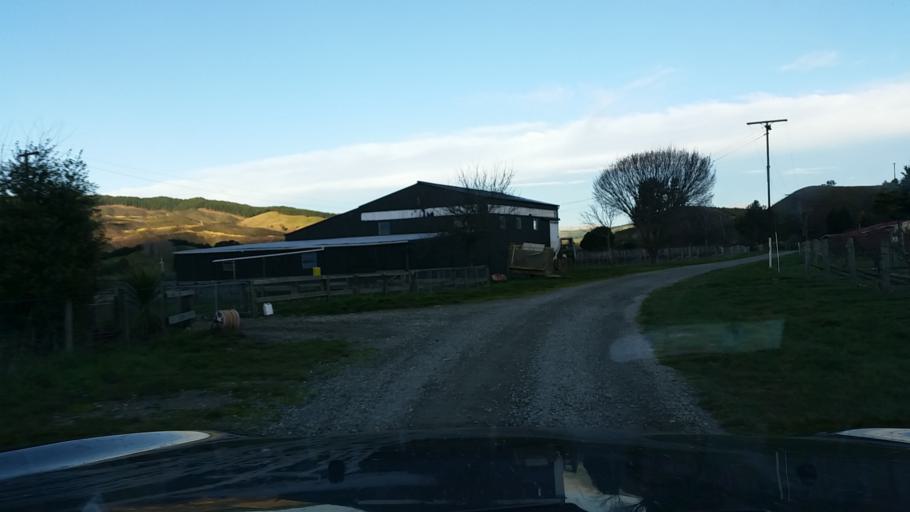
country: NZ
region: Nelson
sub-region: Nelson City
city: Nelson
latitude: -41.5047
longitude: 173.5764
